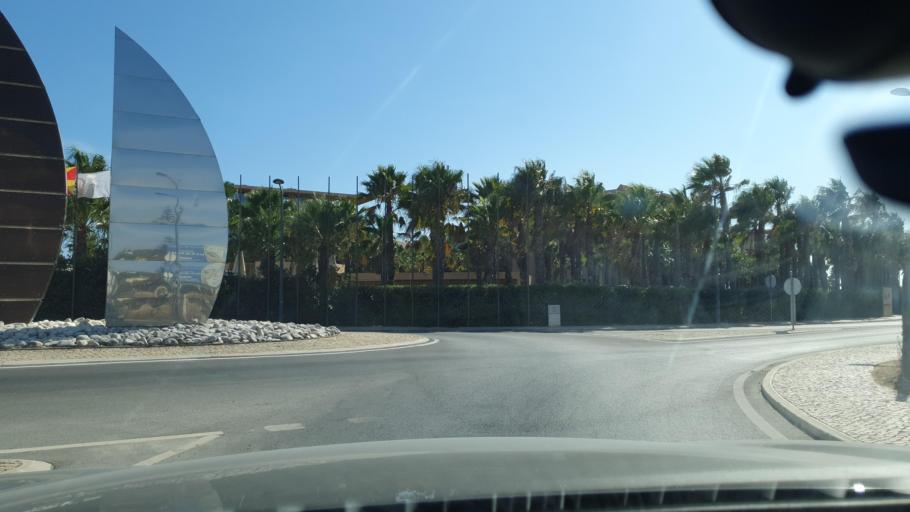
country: PT
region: Faro
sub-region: Silves
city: Armacao de Pera
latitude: 37.0952
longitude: -8.3192
